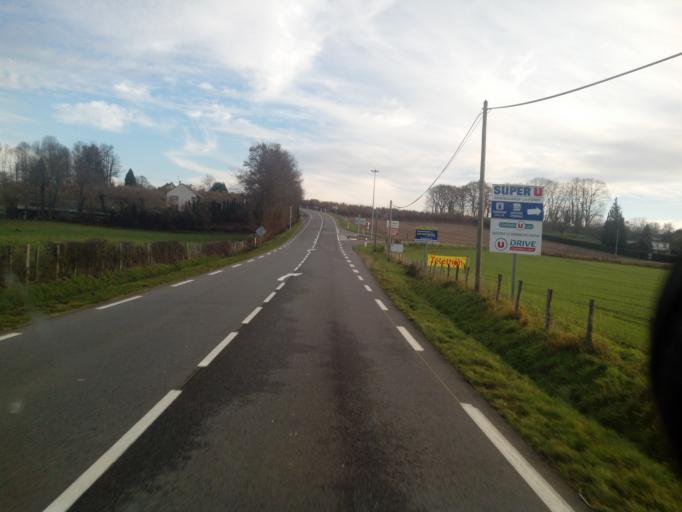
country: FR
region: Limousin
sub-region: Departement de la Haute-Vienne
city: Neuvic-Entier
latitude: 45.7336
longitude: 1.6146
